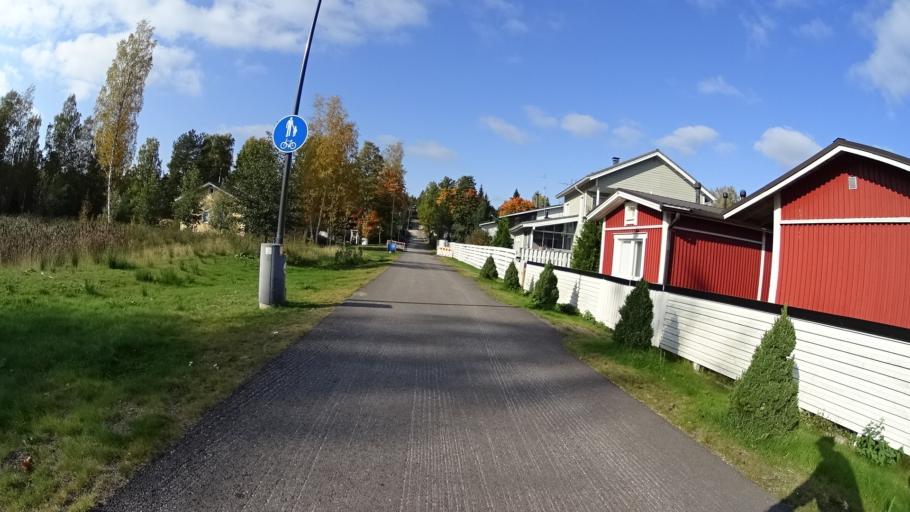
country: FI
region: Uusimaa
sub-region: Helsinki
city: Kilo
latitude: 60.2343
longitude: 24.8052
